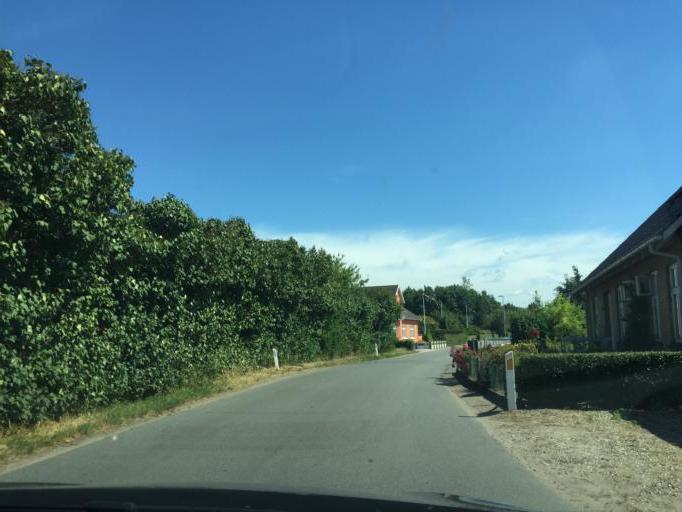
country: DK
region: South Denmark
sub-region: Odense Kommune
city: Bellinge
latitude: 55.3098
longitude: 10.3219
